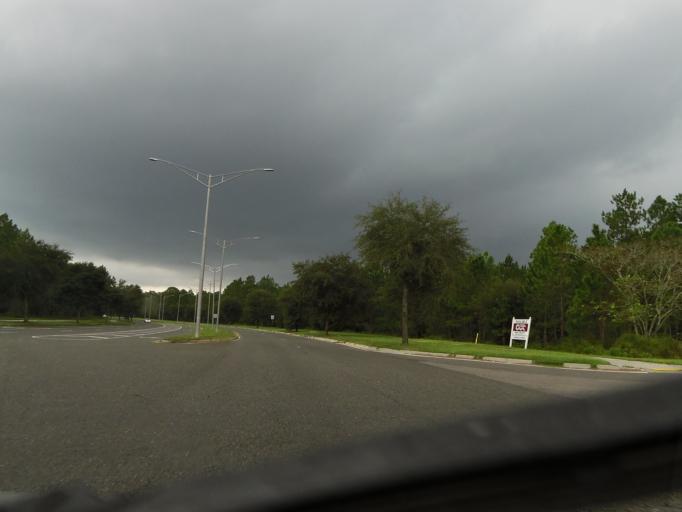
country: US
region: Florida
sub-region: Clay County
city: Lakeside
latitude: 30.1956
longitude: -81.8433
